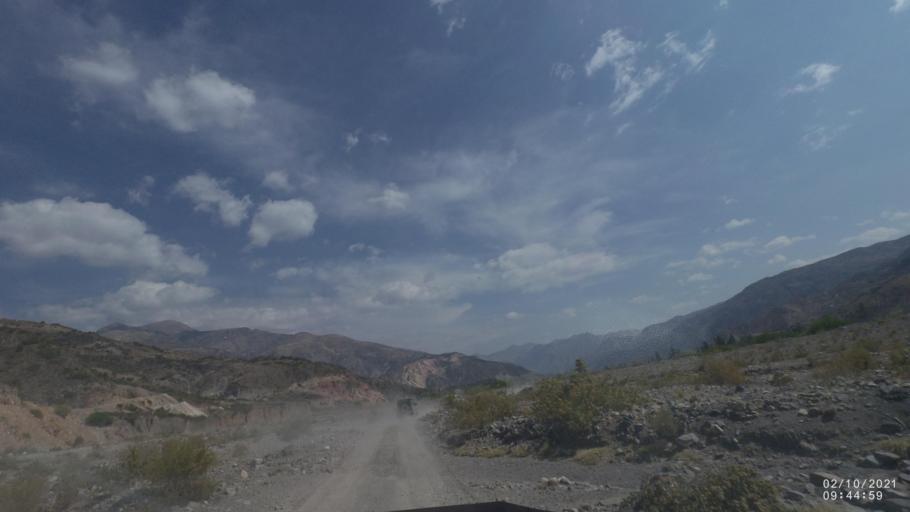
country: BO
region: Cochabamba
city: Irpa Irpa
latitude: -17.8093
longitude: -66.3341
